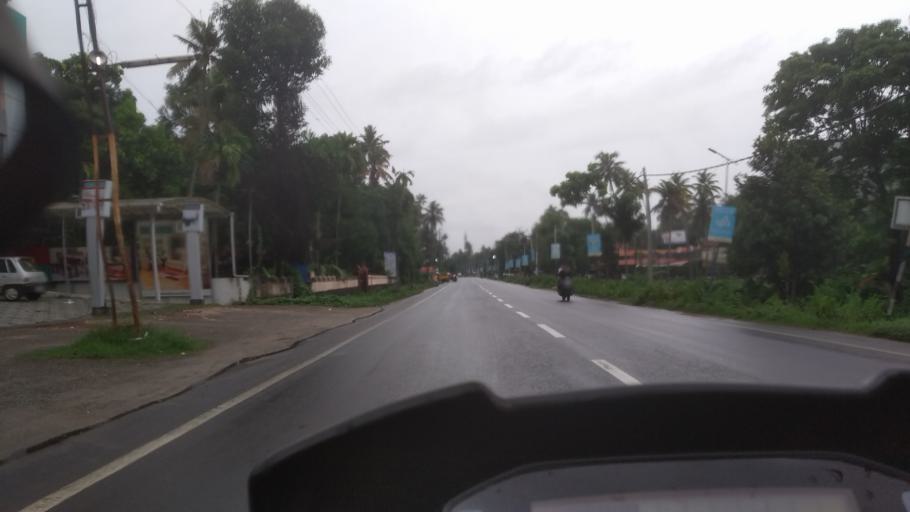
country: IN
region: Kerala
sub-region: Alappuzha
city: Kayankulam
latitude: 9.1321
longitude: 76.5144
